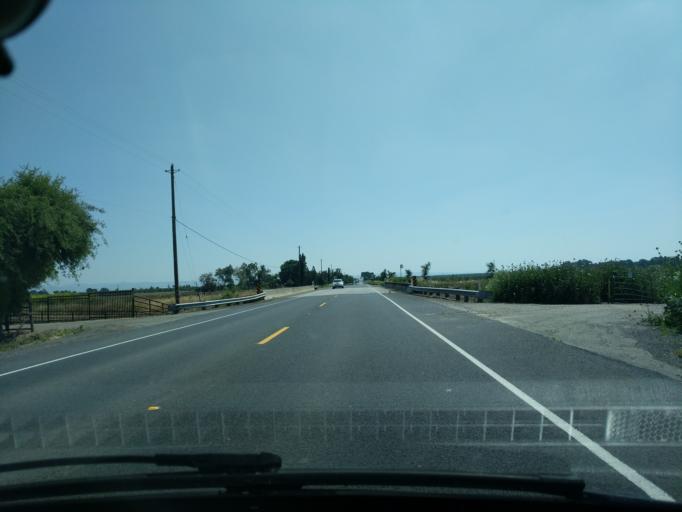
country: US
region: California
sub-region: San Joaquin County
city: Linden
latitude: 37.9301
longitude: -120.9916
